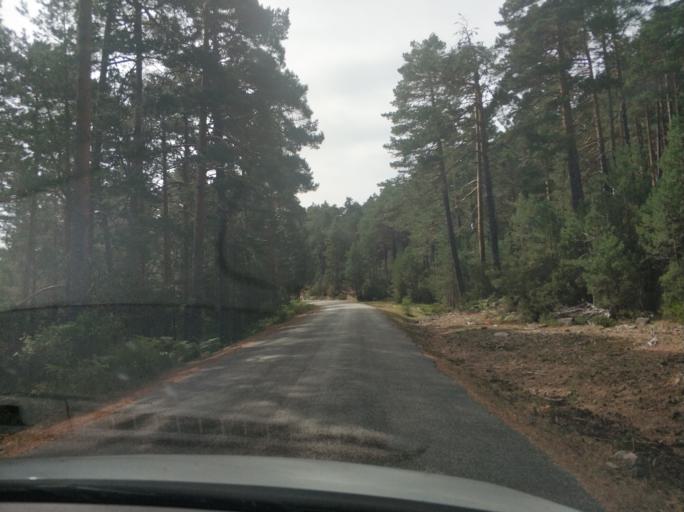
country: ES
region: Castille and Leon
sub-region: Provincia de Soria
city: Duruelo de la Sierra
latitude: 41.9938
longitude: -2.9233
